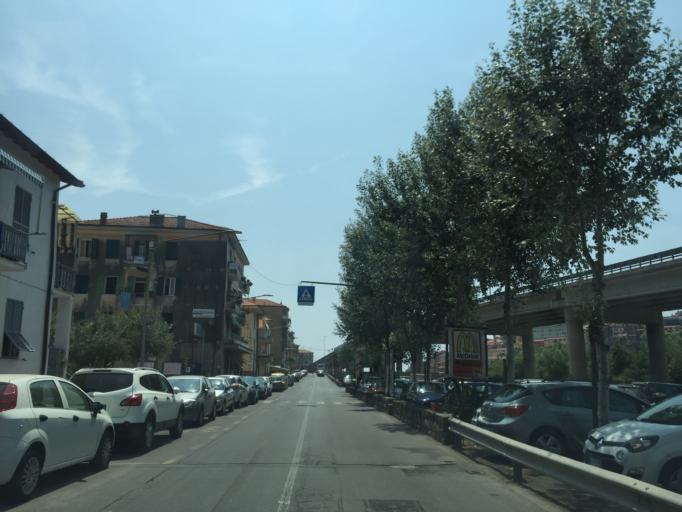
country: IT
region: Liguria
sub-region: Provincia di Imperia
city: Ventimiglia
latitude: 43.7968
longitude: 7.6024
